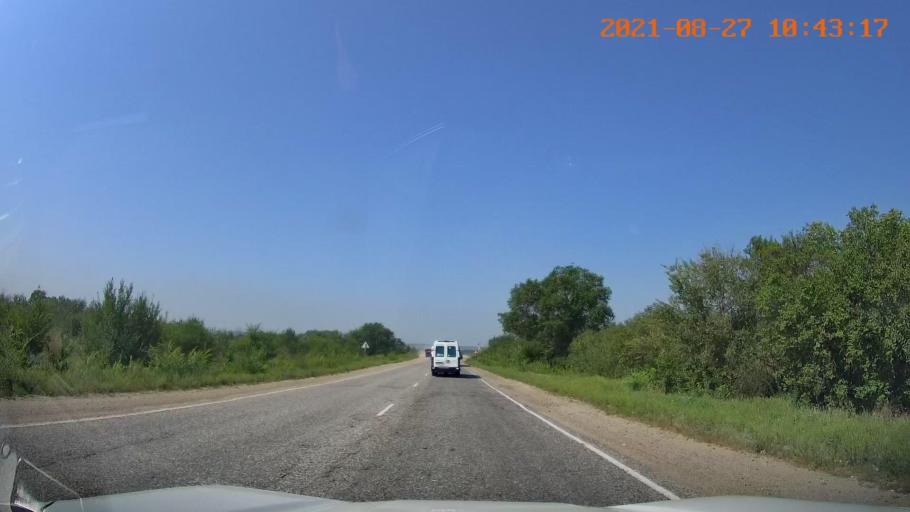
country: RU
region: Karachayevo-Cherkesiya
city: Psyzh
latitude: 44.3007
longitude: 42.0324
